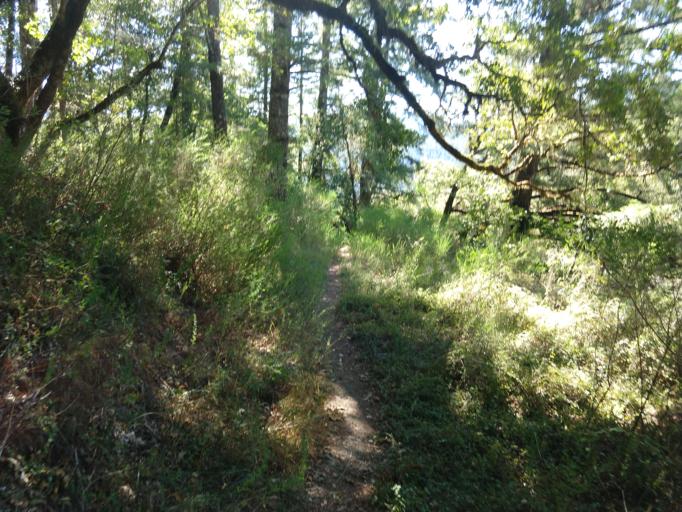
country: US
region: California
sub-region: Humboldt County
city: Rio Dell
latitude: 40.3589
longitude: -123.9976
